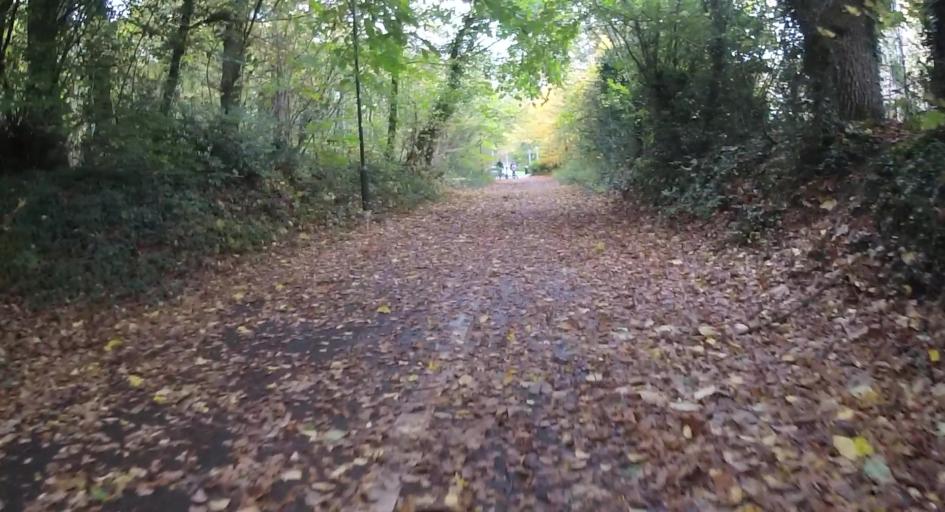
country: GB
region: England
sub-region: Hampshire
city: Old Basing
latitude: 51.2875
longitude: -1.0526
